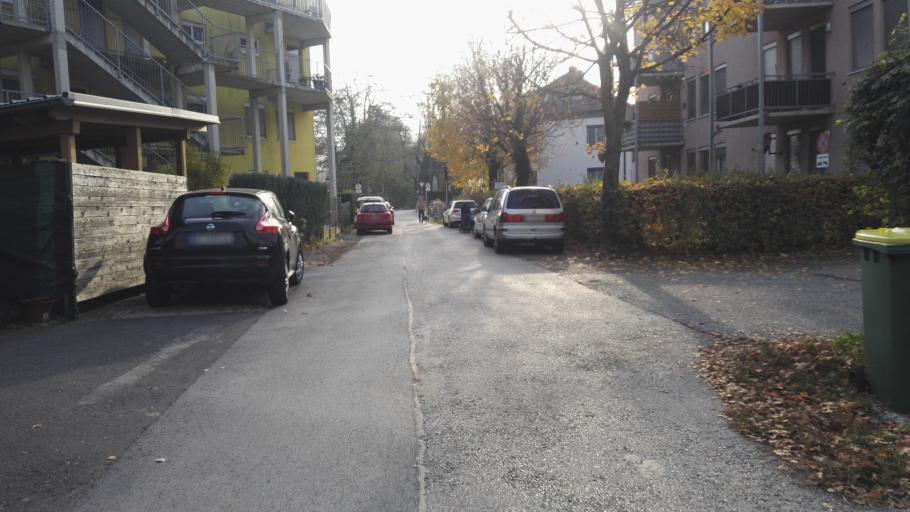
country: AT
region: Styria
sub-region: Graz Stadt
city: Goesting
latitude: 47.0907
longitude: 15.4146
